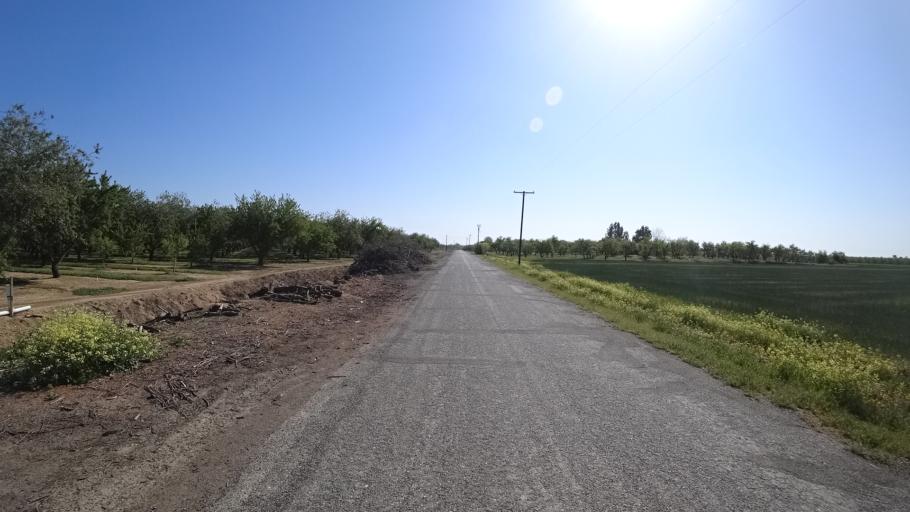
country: US
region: California
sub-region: Glenn County
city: Hamilton City
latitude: 39.6451
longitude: -122.0167
